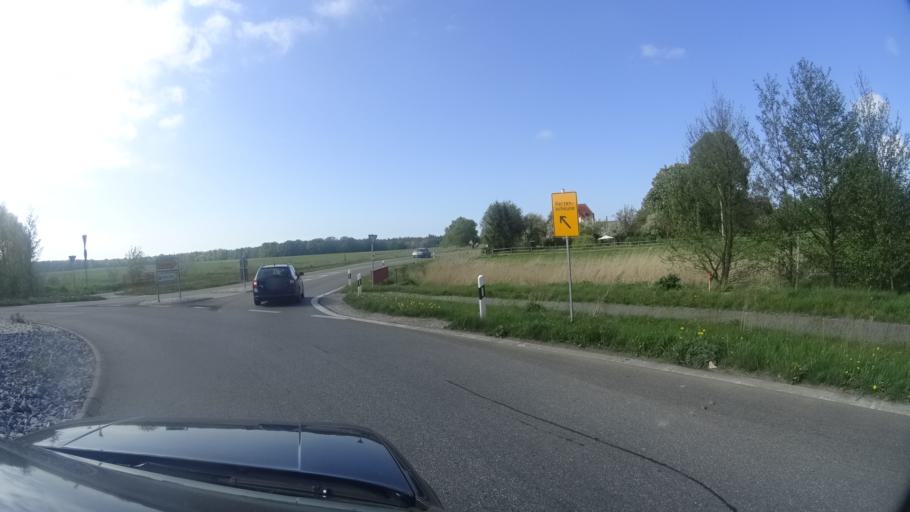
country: DE
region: Mecklenburg-Vorpommern
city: Monchhagen
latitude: 54.1781
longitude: 12.2058
